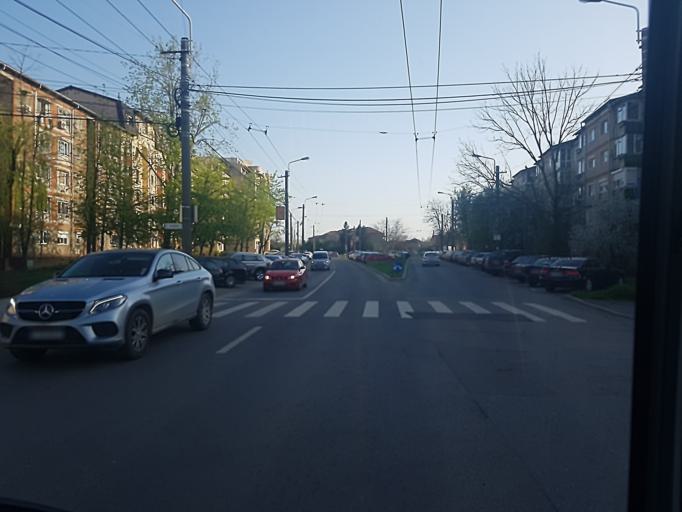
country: RO
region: Timis
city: Timisoara
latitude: 45.7327
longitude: 21.2478
